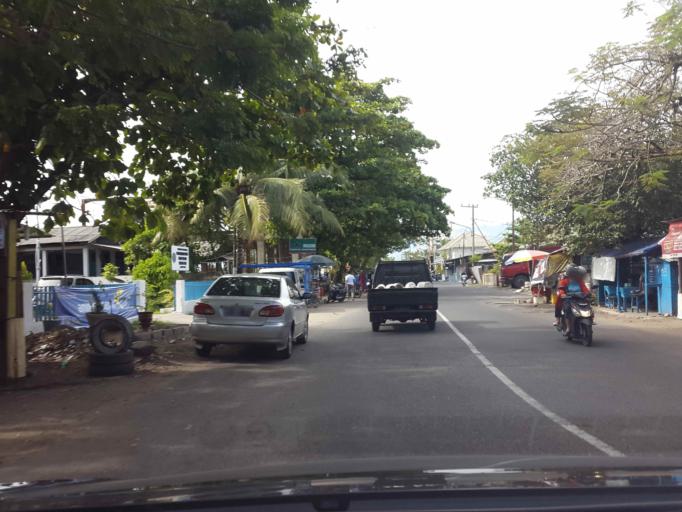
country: ID
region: West Sumatra
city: Padang
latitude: -0.9642
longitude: 100.3519
